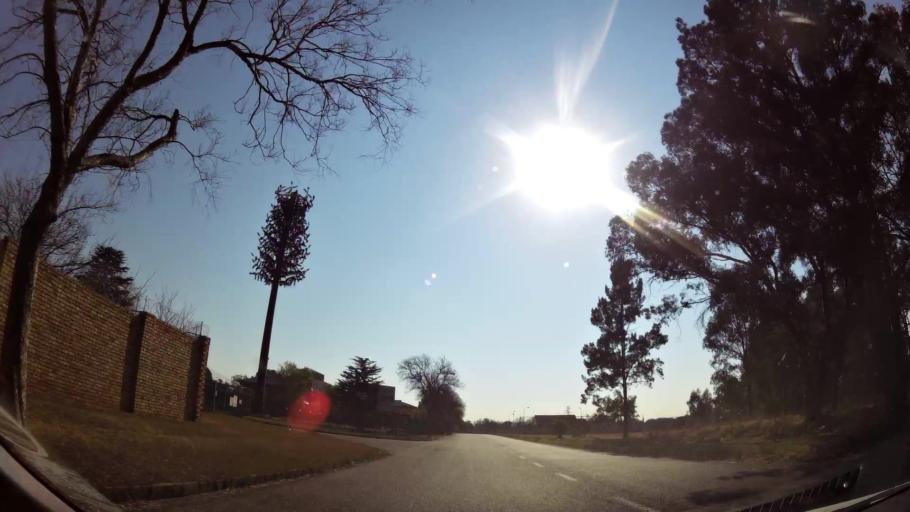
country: ZA
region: Gauteng
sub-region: Ekurhuleni Metropolitan Municipality
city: Boksburg
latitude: -26.2295
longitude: 28.2596
